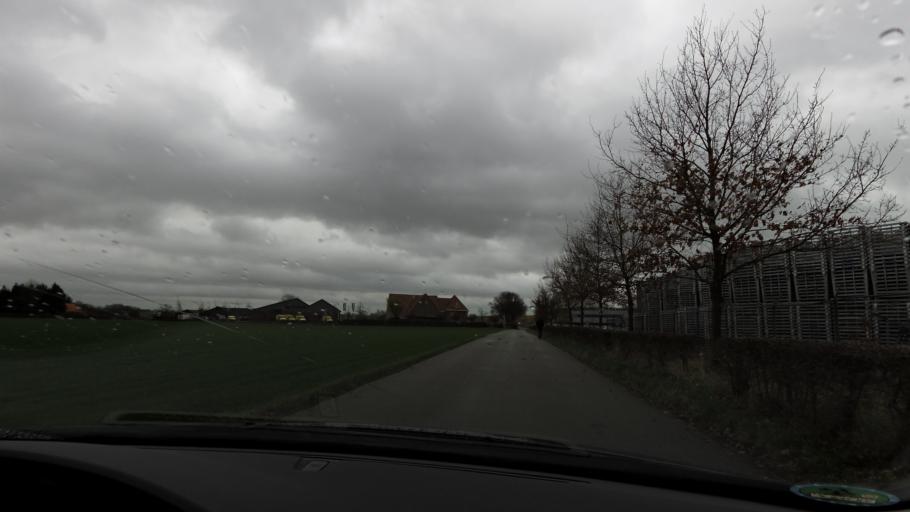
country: NL
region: Limburg
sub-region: Gemeente Beek
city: Beek
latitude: 50.9225
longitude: 5.7902
